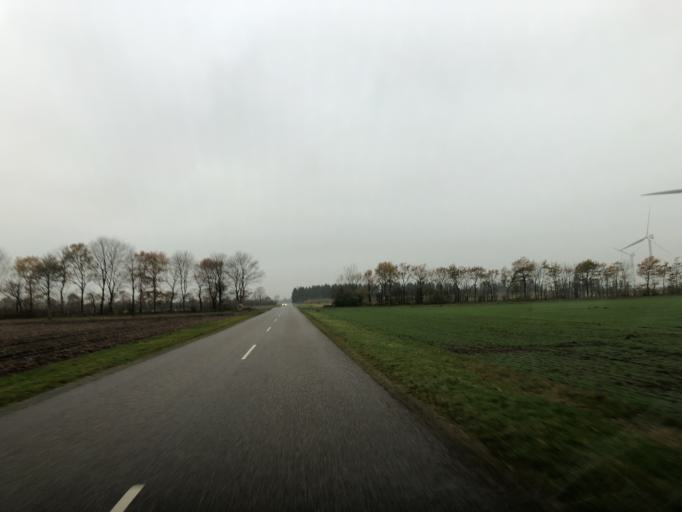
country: DK
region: Central Jutland
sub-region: Herning Kommune
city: Sunds
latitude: 56.2149
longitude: 8.9755
